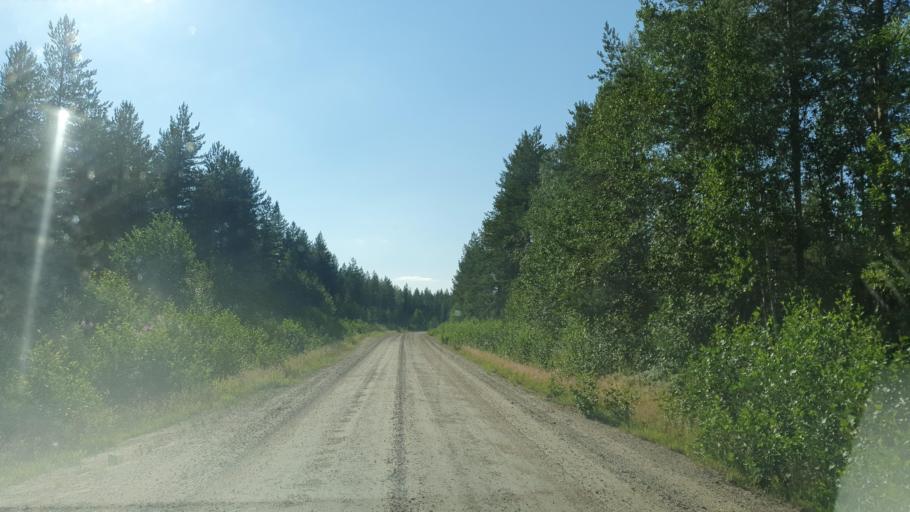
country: FI
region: Kainuu
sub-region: Kehys-Kainuu
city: Kuhmo
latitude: 64.0284
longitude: 29.7034
